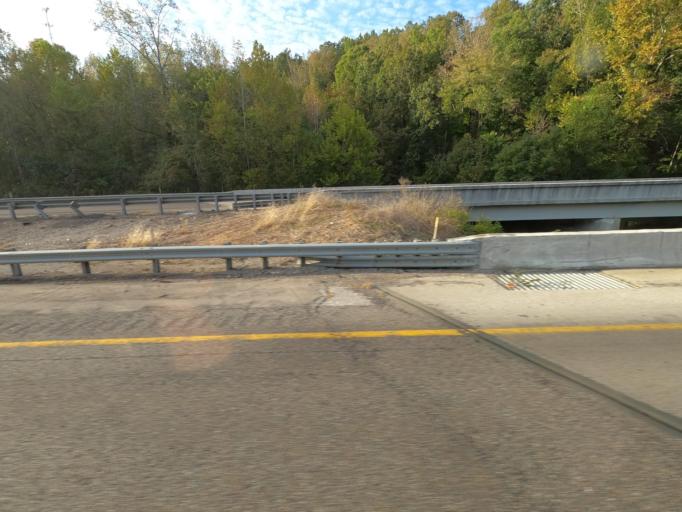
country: US
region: Tennessee
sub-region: Humphreys County
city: New Johnsonville
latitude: 35.8694
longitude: -87.8660
